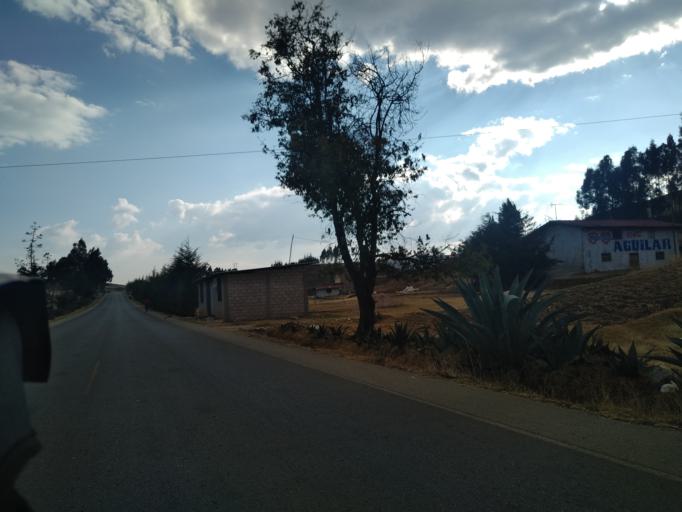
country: PE
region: Cajamarca
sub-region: Provincia de Cajamarca
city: Llacanora
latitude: -7.1440
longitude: -78.3931
